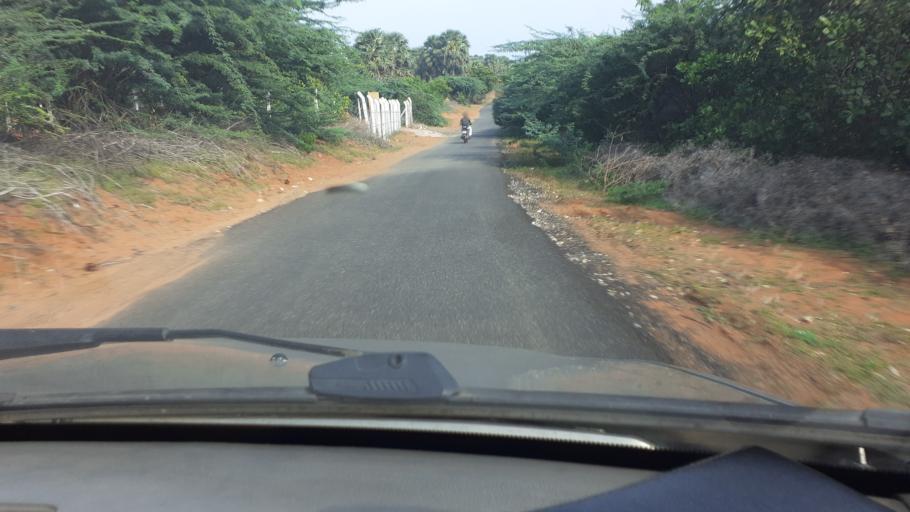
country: IN
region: Tamil Nadu
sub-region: Tirunelveli Kattabo
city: Tisaiyanvilai
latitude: 8.3377
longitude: 77.9448
